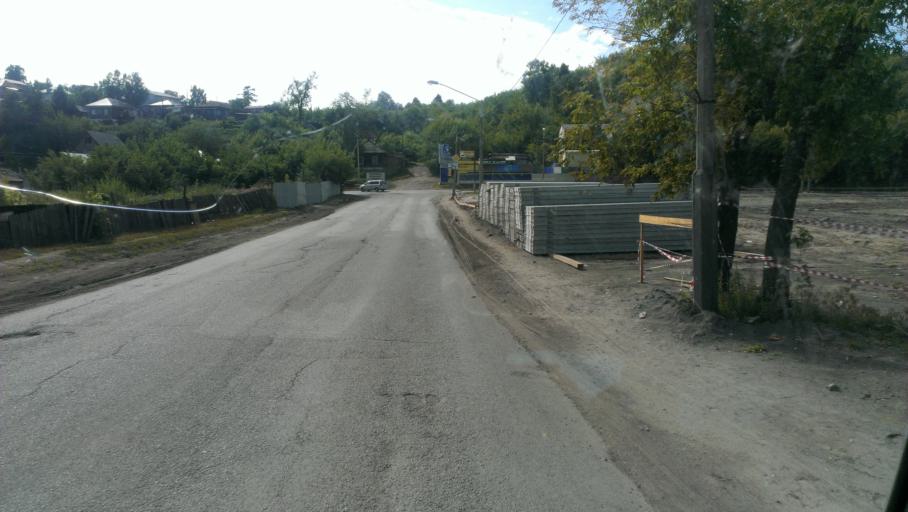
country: RU
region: Altai Krai
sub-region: Gorod Barnaulskiy
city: Barnaul
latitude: 53.3200
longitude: 83.7700
